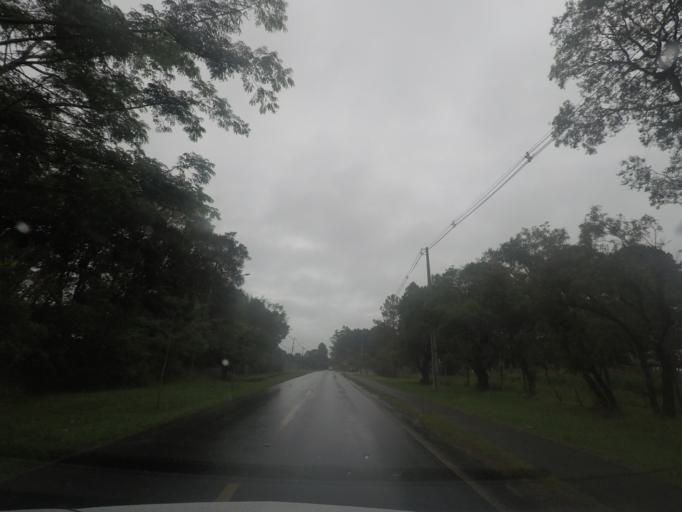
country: BR
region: Parana
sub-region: Quatro Barras
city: Quatro Barras
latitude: -25.3725
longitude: -49.0884
